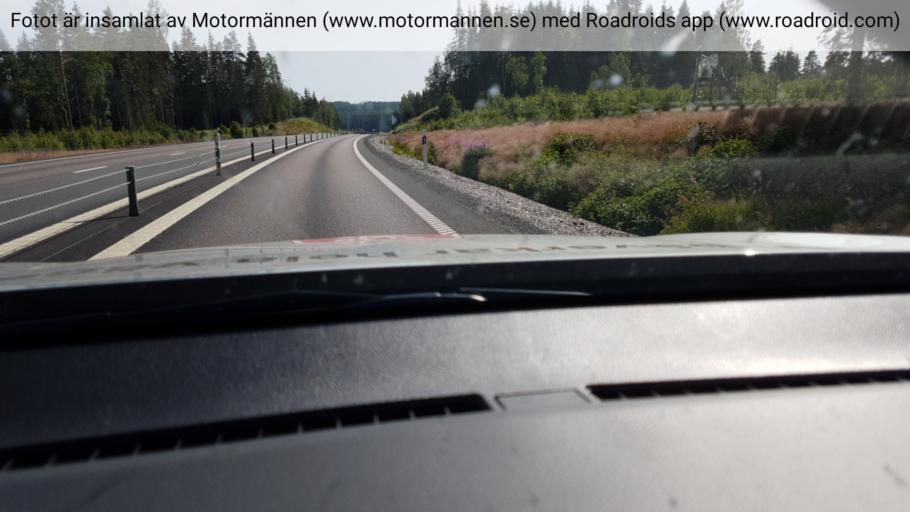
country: SE
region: Joenkoeping
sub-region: Aneby Kommun
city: Aneby
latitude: 57.8269
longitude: 14.8711
